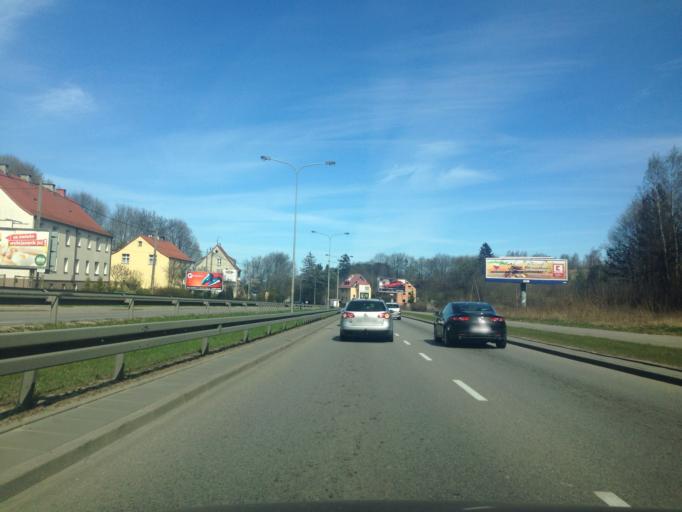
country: PL
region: Pomeranian Voivodeship
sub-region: Powiat gdanski
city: Kowale
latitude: 54.3708
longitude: 18.5613
